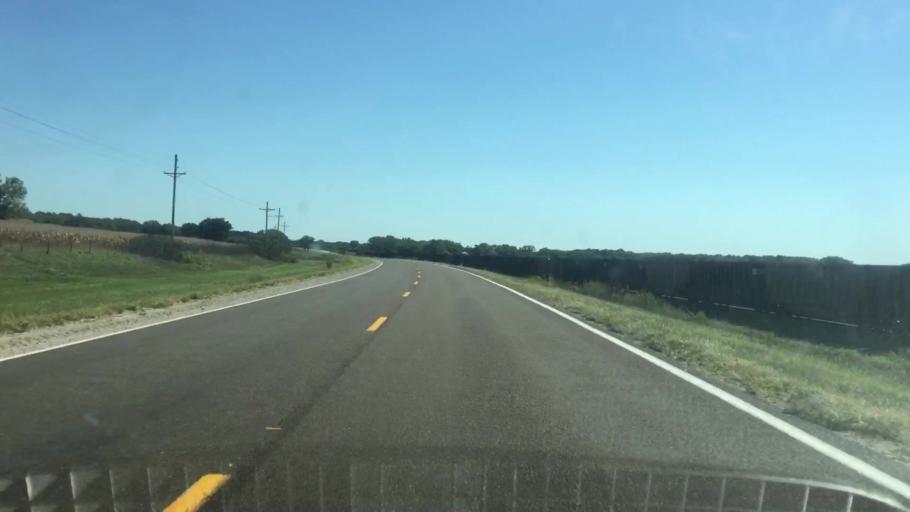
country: US
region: Nebraska
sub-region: Jefferson County
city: Fairbury
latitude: 40.0861
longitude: -97.1170
